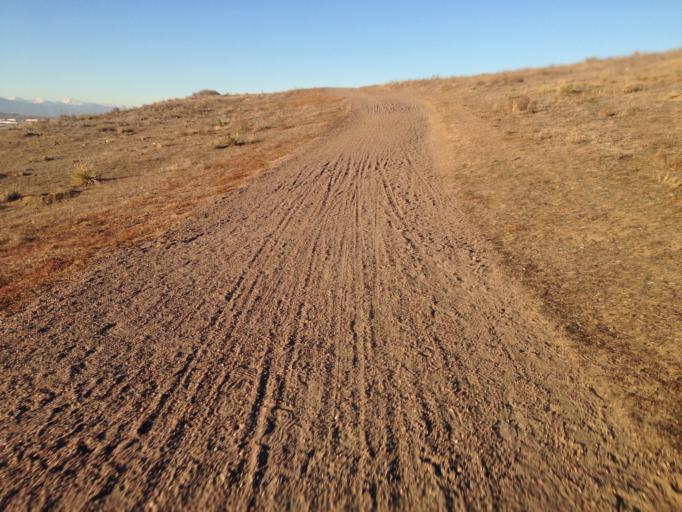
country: US
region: Colorado
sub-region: Broomfield County
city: Broomfield
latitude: 39.9393
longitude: -105.0872
